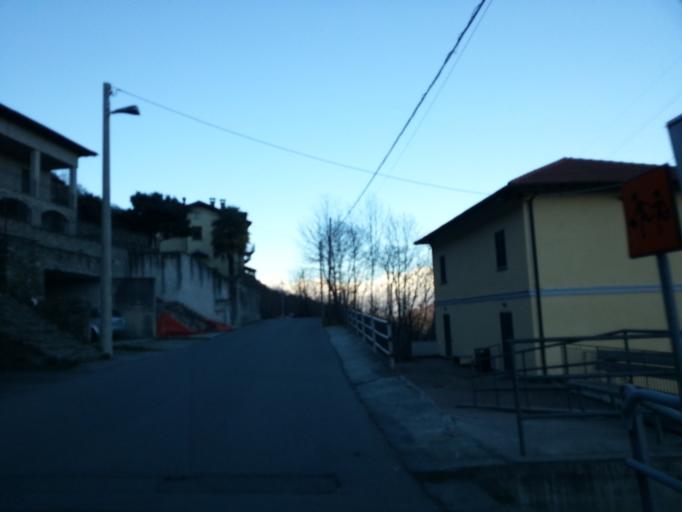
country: IT
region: Lombardy
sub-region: Provincia di Como
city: San Siro
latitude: 46.0688
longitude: 9.2606
